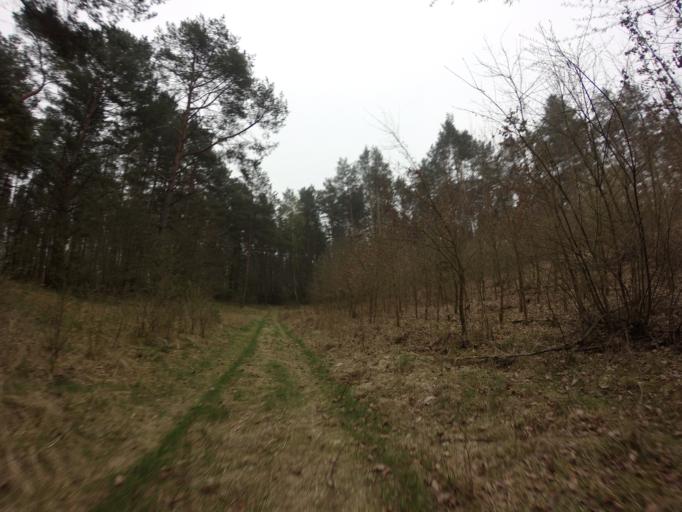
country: PL
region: West Pomeranian Voivodeship
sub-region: Powiat choszczenski
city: Recz
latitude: 53.1925
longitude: 15.5383
